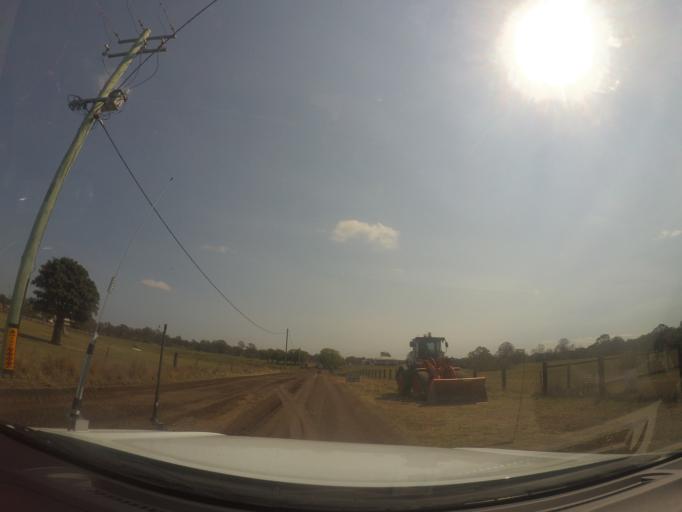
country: AU
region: Queensland
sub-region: Logan
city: Chambers Flat
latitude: -27.7573
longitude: 153.0598
